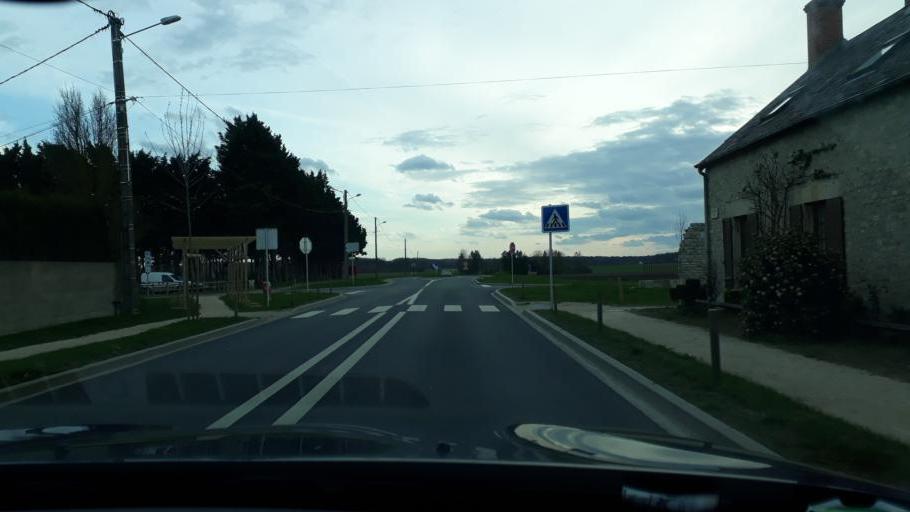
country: FR
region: Centre
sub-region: Departement du Loiret
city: Chilleurs-aux-Bois
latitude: 48.0674
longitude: 2.1322
